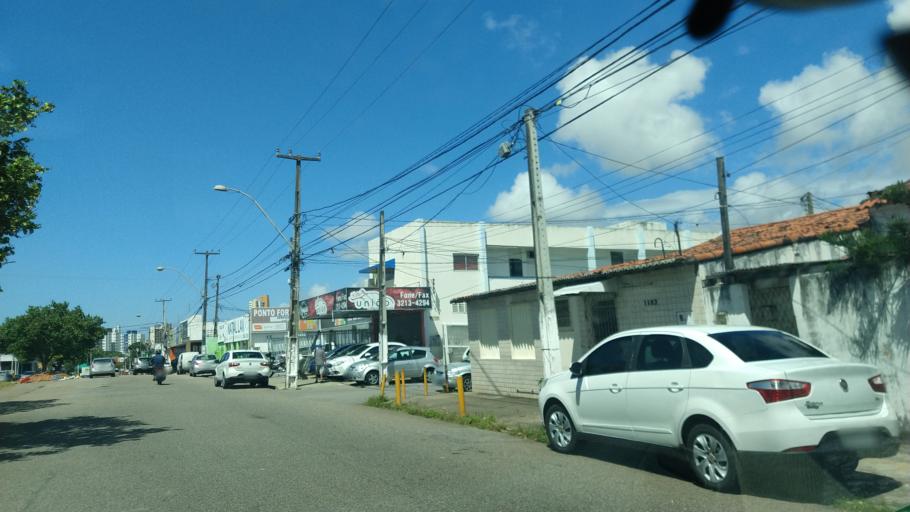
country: BR
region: Rio Grande do Norte
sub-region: Natal
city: Natal
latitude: -5.8071
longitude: -35.2127
